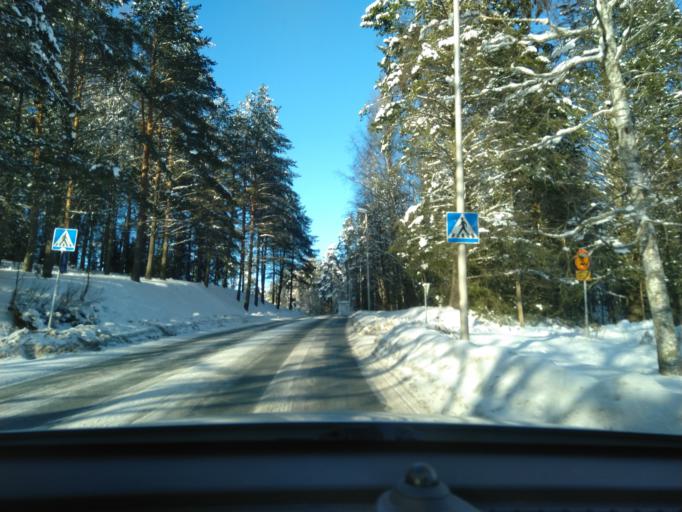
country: FI
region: Haeme
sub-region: Haemeenlinna
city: Haemeenlinna
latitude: 60.9876
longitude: 24.4175
